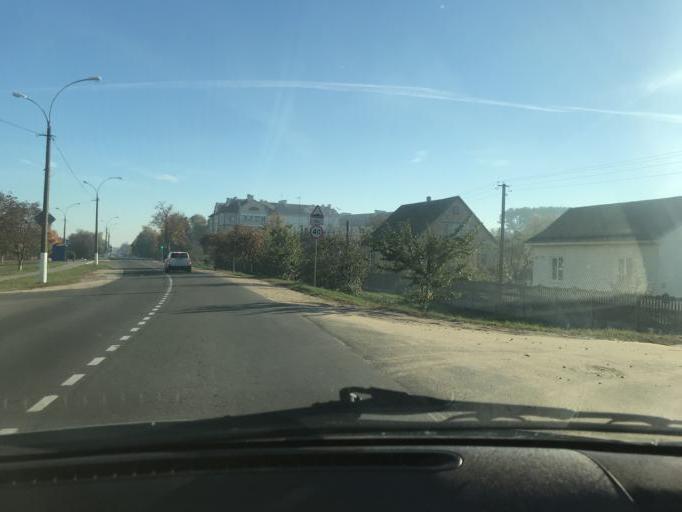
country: BY
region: Brest
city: Ivanava
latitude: 52.1431
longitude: 25.5235
